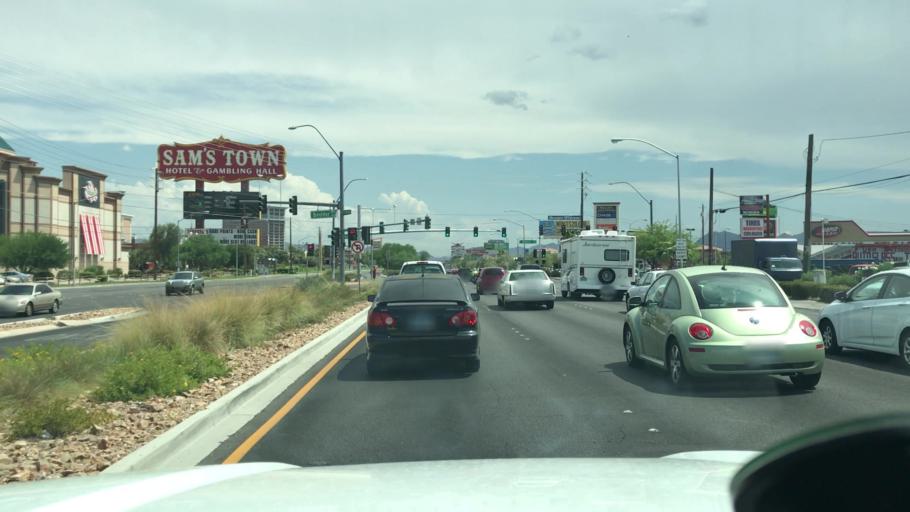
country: US
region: Nevada
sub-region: Clark County
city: Whitney
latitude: 36.1134
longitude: -115.0652
